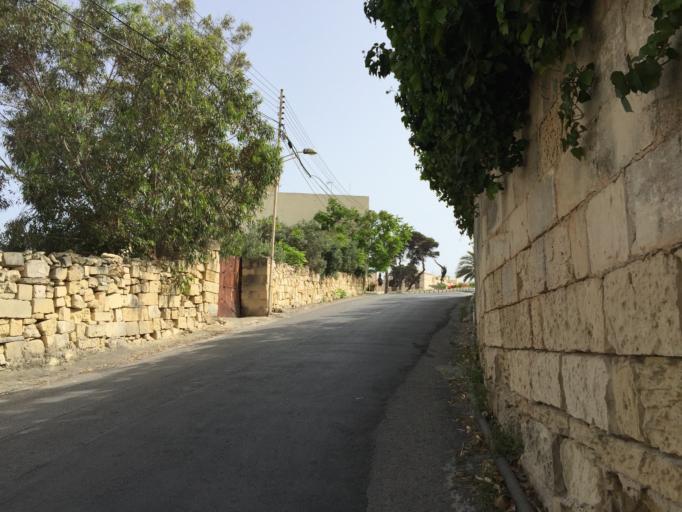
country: MT
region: Il-Kalkara
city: Kalkara
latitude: 35.8923
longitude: 14.5269
